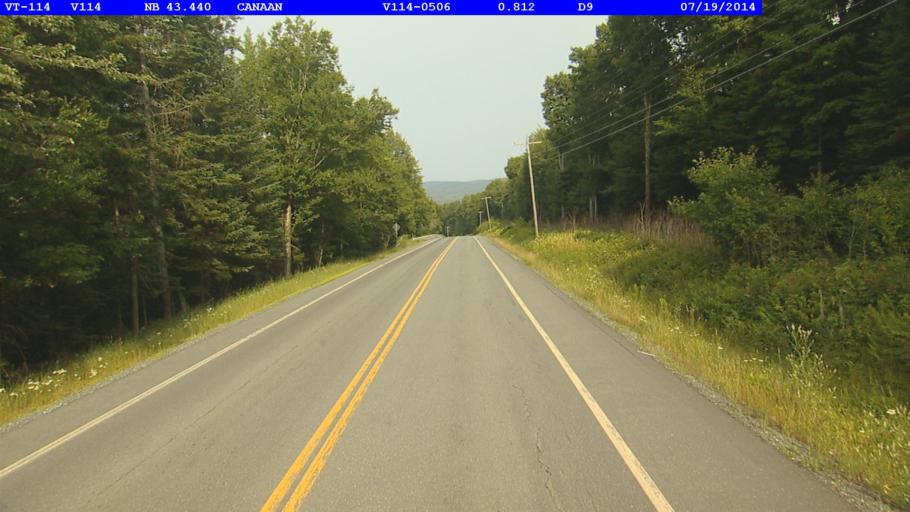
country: CA
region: Quebec
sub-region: Estrie
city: Coaticook
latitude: 45.0060
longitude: -71.6773
